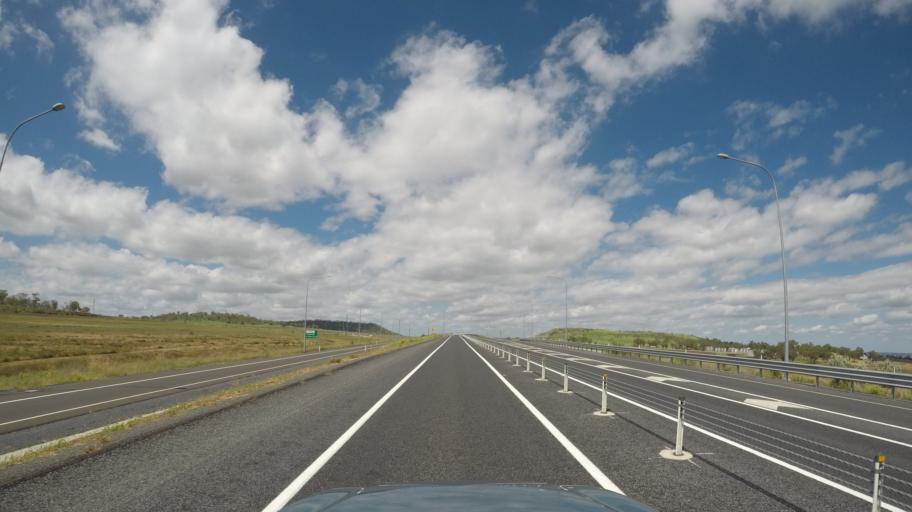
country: AU
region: Queensland
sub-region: Toowoomba
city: Westbrook
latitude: -27.5443
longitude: 151.8373
